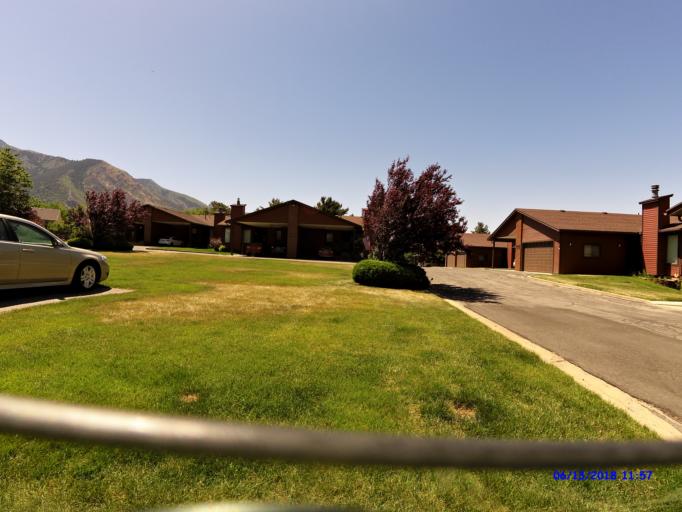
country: US
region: Utah
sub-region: Weber County
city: Ogden
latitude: 41.2317
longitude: -111.9449
